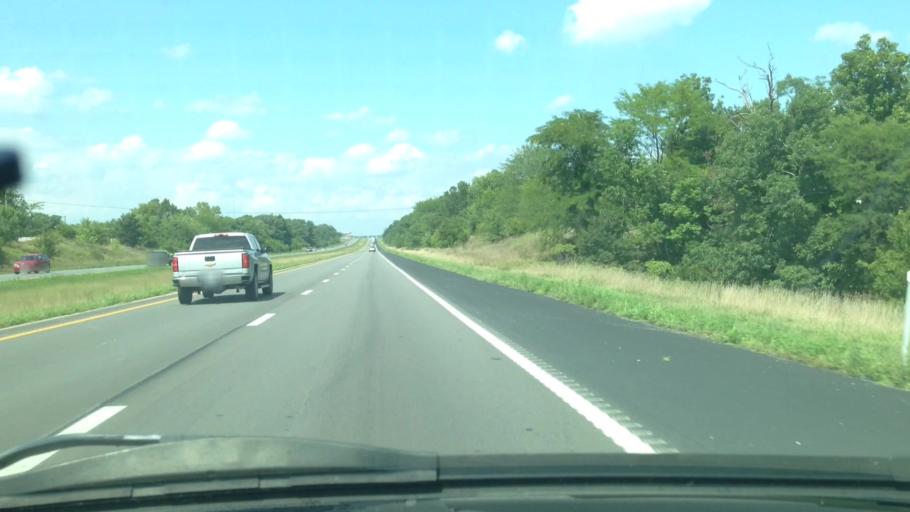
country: US
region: Missouri
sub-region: Lincoln County
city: Troy
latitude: 39.0519
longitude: -90.9739
